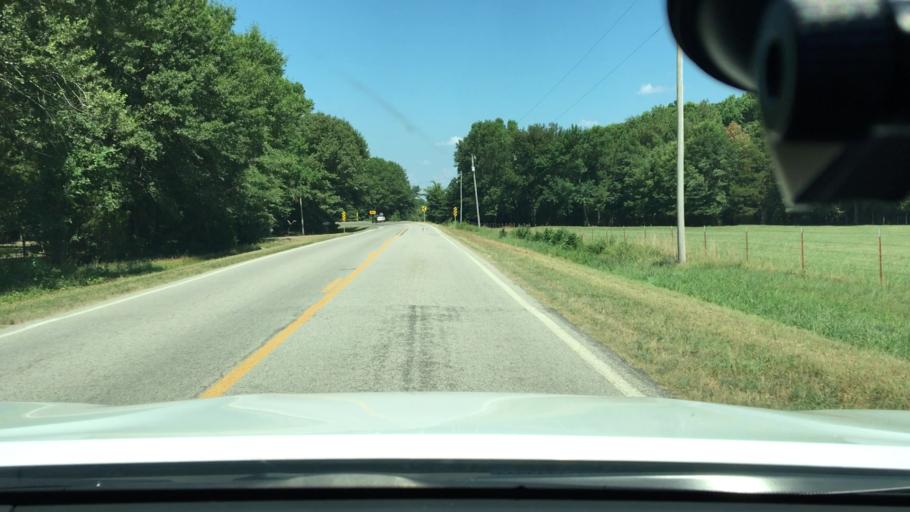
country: US
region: Arkansas
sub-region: Johnson County
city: Clarksville
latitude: 35.3573
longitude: -93.5516
